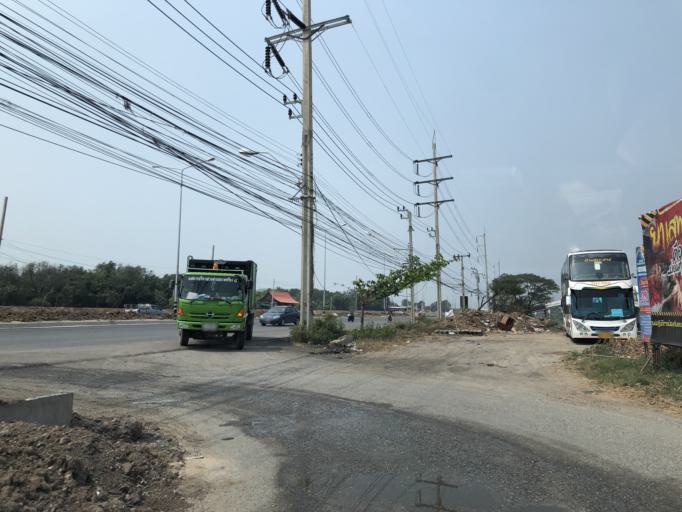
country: TH
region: Samut Prakan
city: Bang Bo
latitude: 13.5101
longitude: 100.8050
